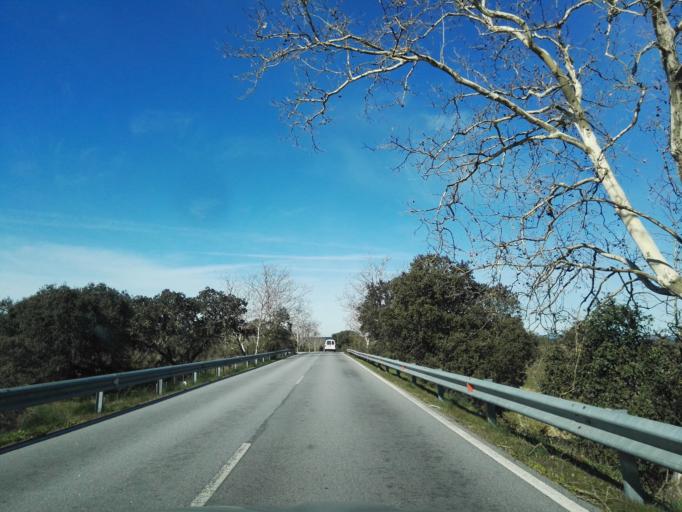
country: PT
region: Portalegre
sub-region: Arronches
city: Arronches
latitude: 39.0454
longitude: -7.2626
